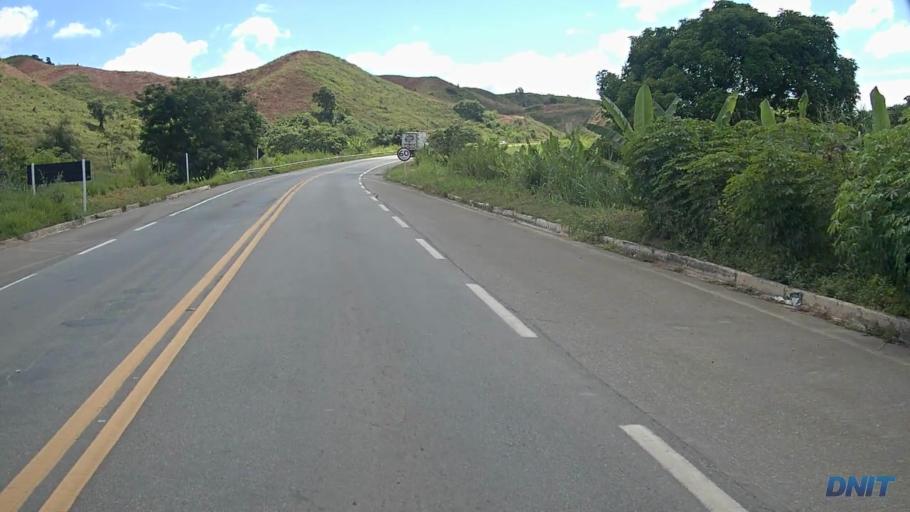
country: BR
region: Minas Gerais
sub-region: Belo Oriente
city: Belo Oriente
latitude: -19.1484
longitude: -42.2321
